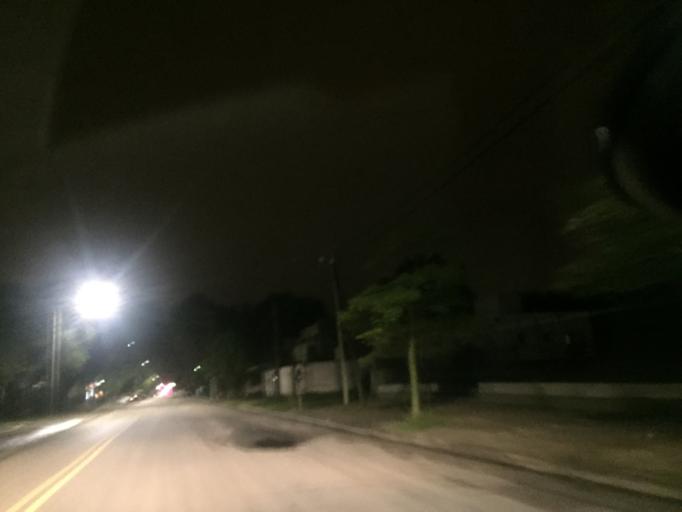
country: AR
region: Cordoba
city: Villa Allende
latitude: -31.3024
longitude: -64.2882
